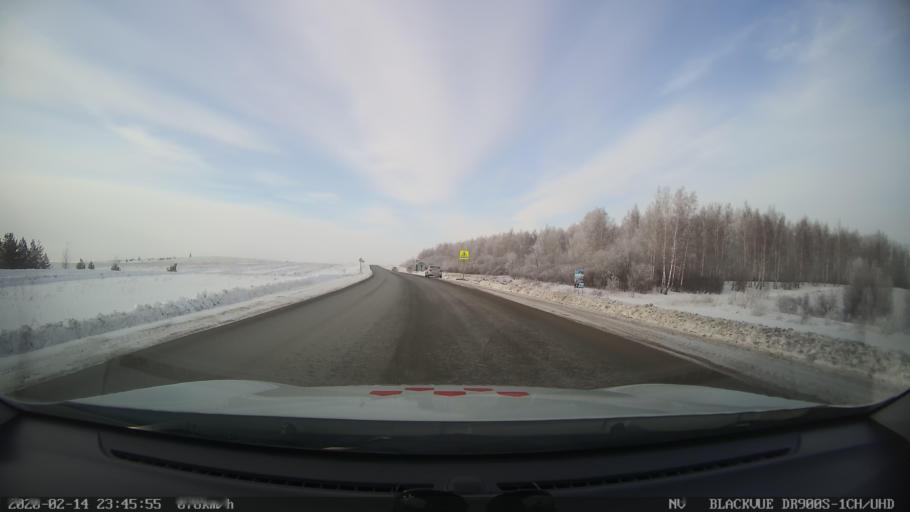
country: RU
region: Tatarstan
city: Kuybyshevskiy Zaton
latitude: 55.2264
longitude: 49.2319
